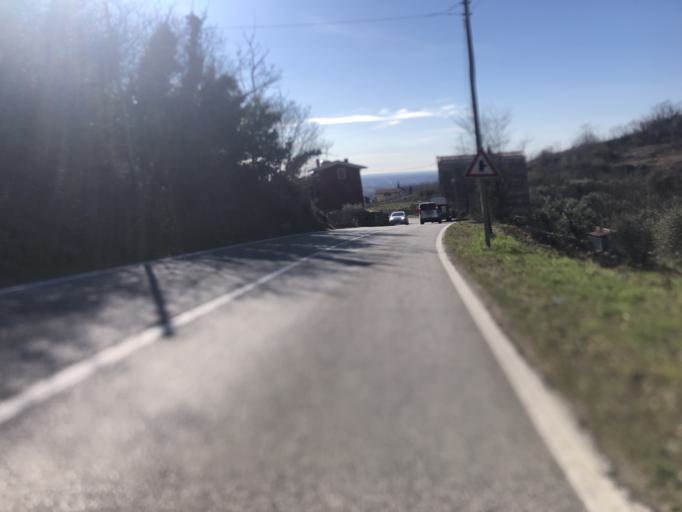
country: IT
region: Veneto
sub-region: Provincia di Verona
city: Sant'Ambrogio di Valpollicella
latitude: 45.5324
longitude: 10.8340
